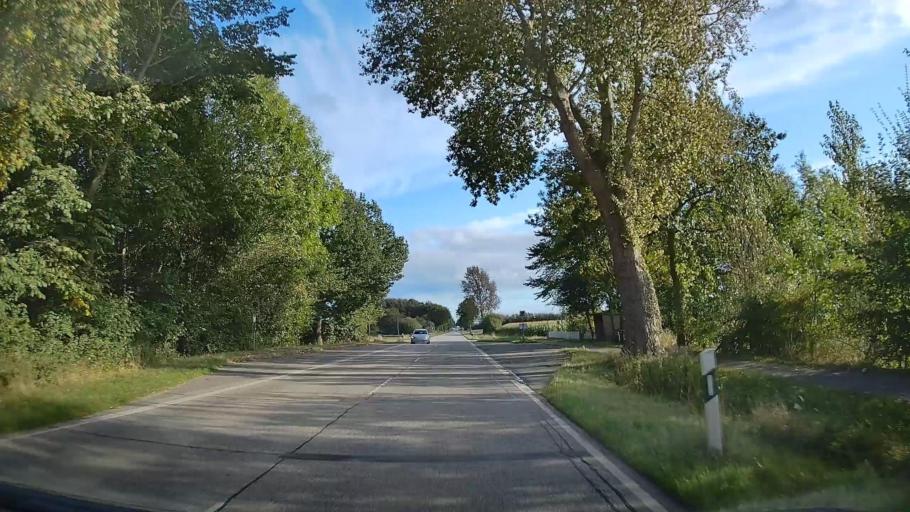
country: DE
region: Schleswig-Holstein
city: Rabel
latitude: 54.7318
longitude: 9.9424
